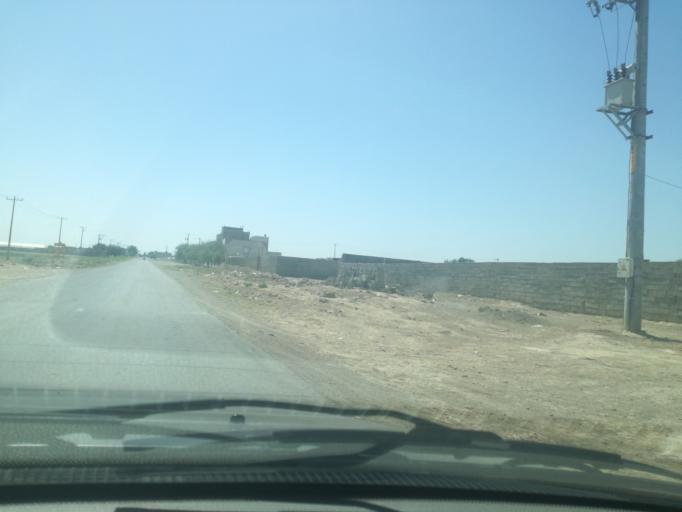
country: IR
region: Razavi Khorasan
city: Sarakhs
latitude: 36.5665
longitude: 61.1415
